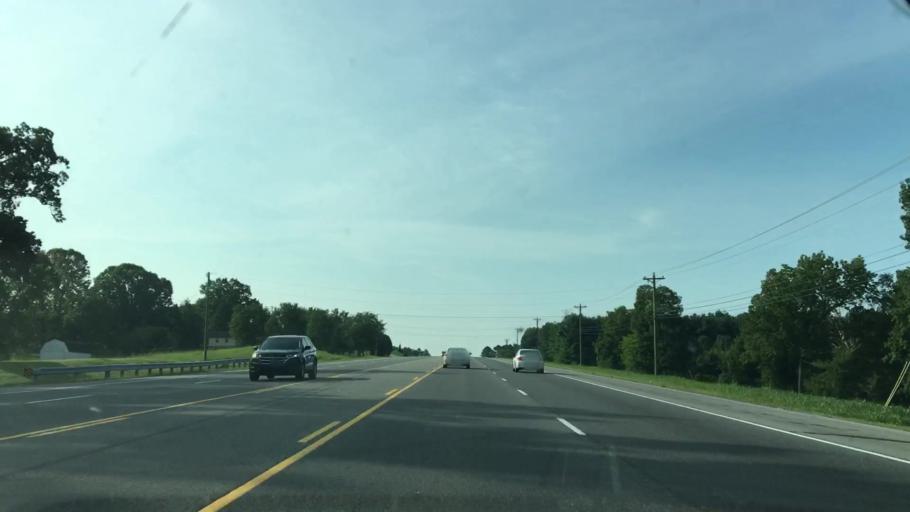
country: US
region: Tennessee
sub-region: Wilson County
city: Mount Juliet
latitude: 36.2140
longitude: -86.4220
